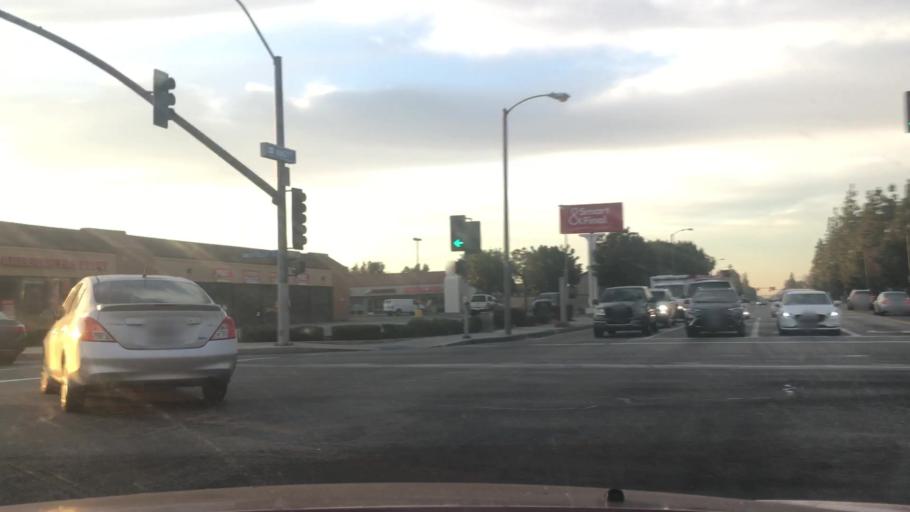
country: US
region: California
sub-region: Orange County
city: Stanton
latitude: 33.8030
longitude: -118.0110
